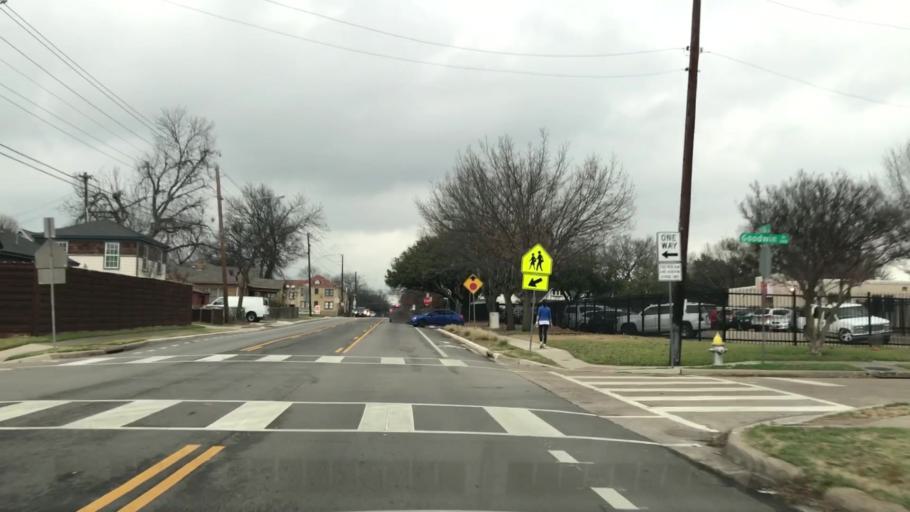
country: US
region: Texas
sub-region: Dallas County
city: Highland Park
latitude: 32.8237
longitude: -96.7680
